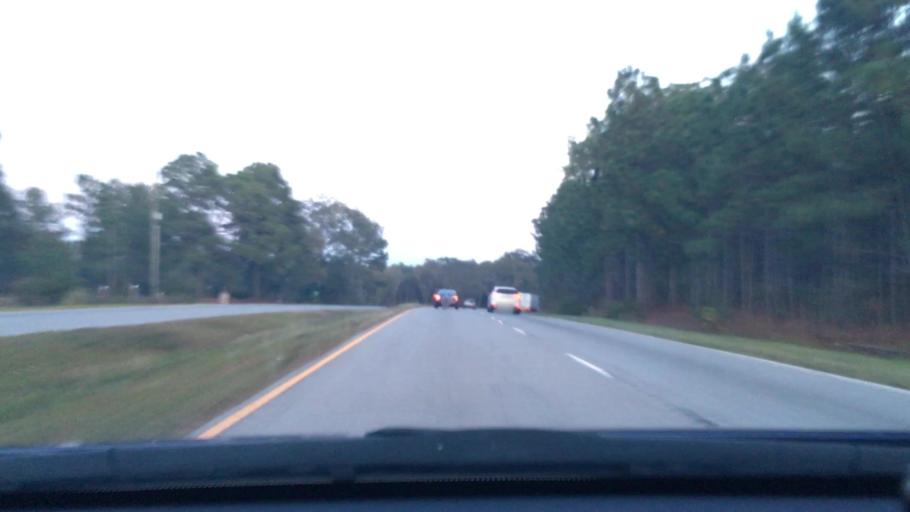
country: US
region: South Carolina
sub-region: Richland County
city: Gadsden
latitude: 33.9435
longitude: -80.6712
